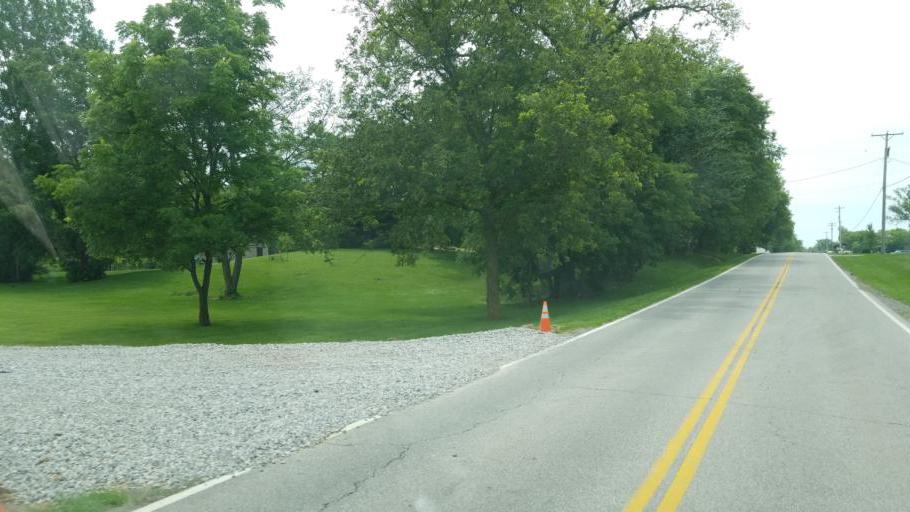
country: US
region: Ohio
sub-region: Madison County
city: Plain City
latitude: 40.0775
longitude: -83.2528
